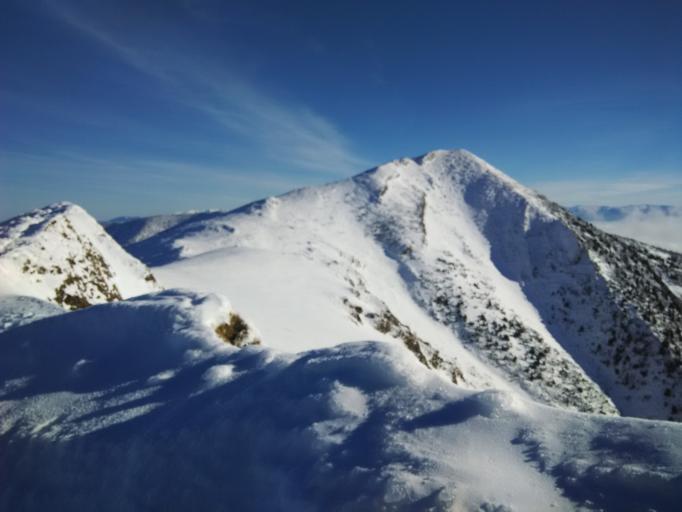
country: SK
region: Zilinsky
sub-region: Okres Zilina
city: Terchova
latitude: 49.1908
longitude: 19.0187
